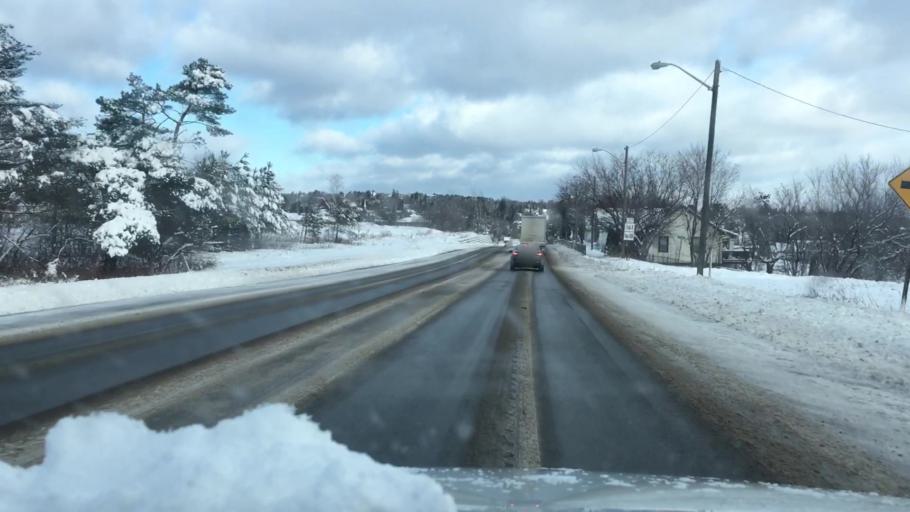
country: US
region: Maine
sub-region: Aroostook County
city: Caribou
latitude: 46.8512
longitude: -68.0052
